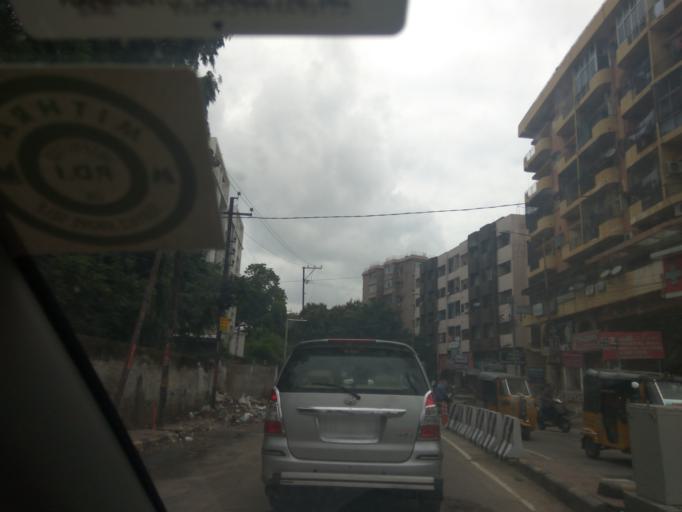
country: IN
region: Telangana
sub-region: Hyderabad
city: Hyderabad
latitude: 17.3938
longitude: 78.4800
